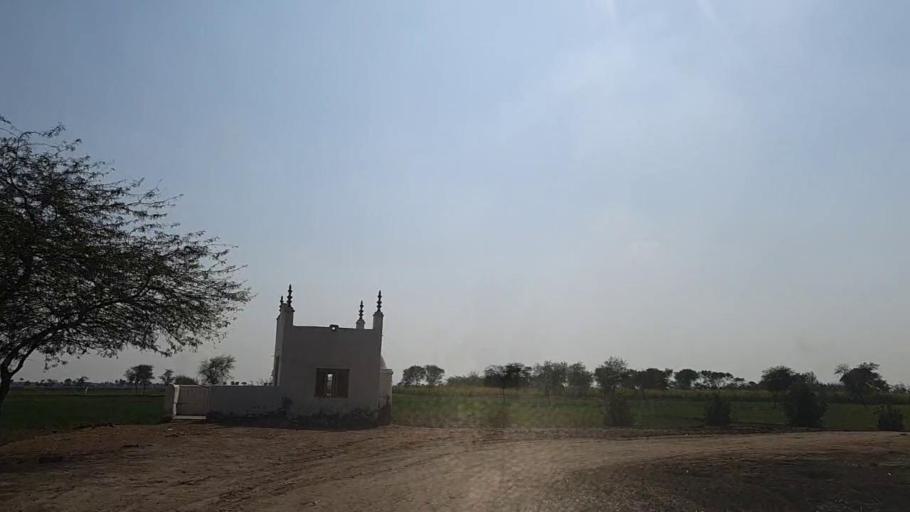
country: PK
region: Sindh
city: Daur
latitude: 26.4524
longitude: 68.2425
